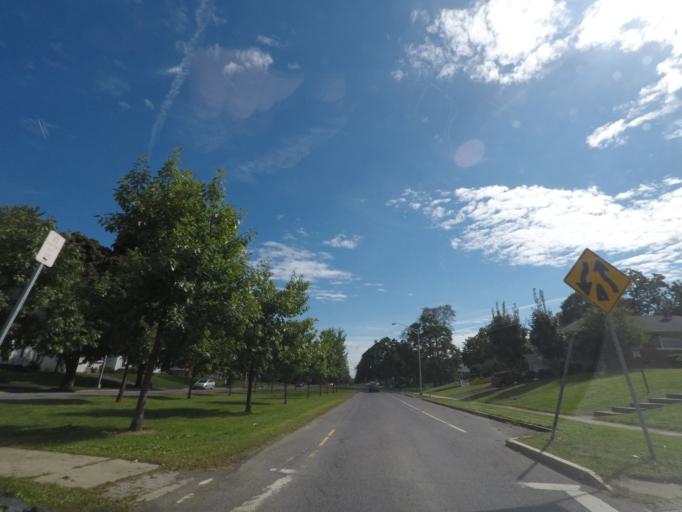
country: US
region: New York
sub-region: Albany County
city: West Albany
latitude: 42.6508
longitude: -73.8001
